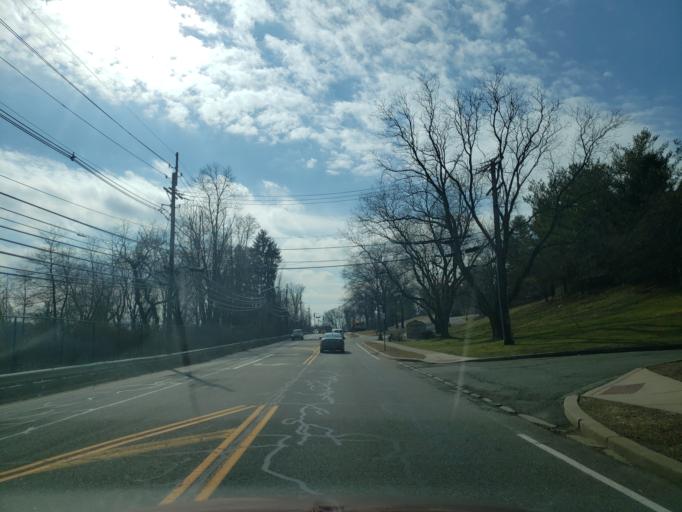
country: US
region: New Jersey
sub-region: Essex County
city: West Orange
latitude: 40.7881
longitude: -74.2731
